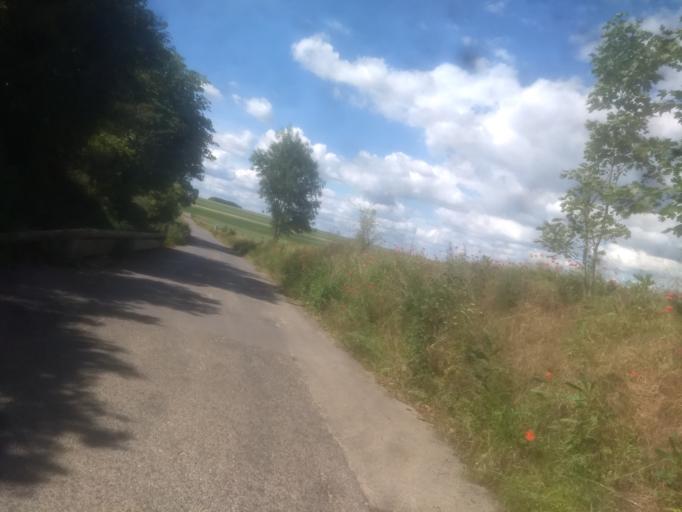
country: FR
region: Nord-Pas-de-Calais
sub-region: Departement du Pas-de-Calais
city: Tilloy-les-Mofflaines
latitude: 50.2510
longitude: 2.8232
